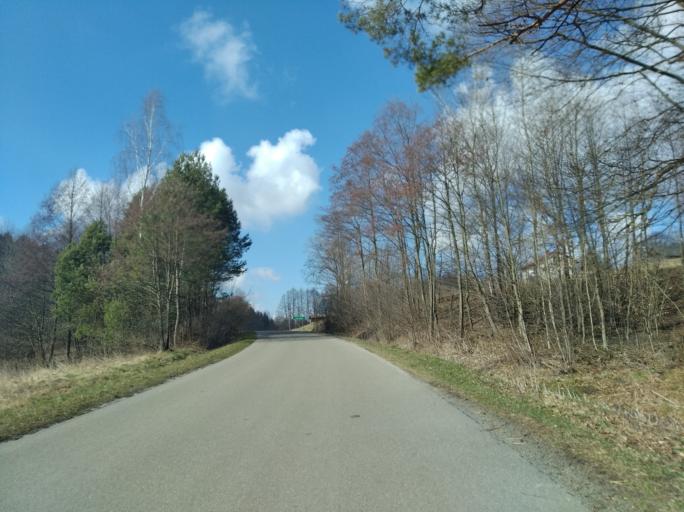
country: PL
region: Subcarpathian Voivodeship
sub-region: Powiat strzyzowski
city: Frysztak
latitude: 49.8668
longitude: 21.5417
